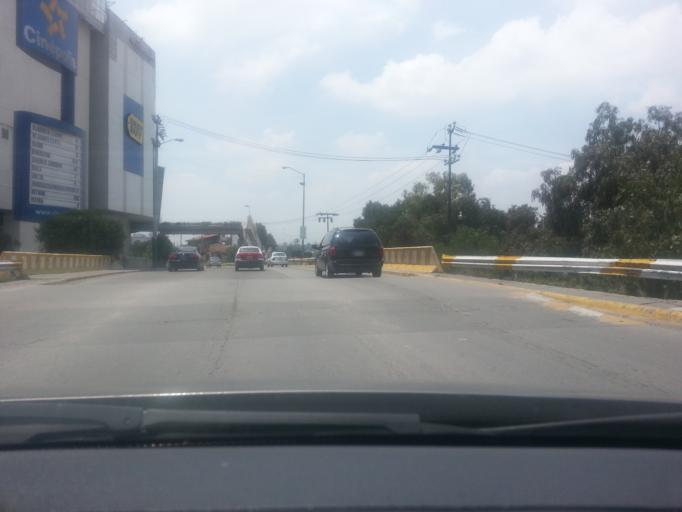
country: MX
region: Mexico
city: Cuautitlan Izcalli
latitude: 19.6586
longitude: -99.2099
